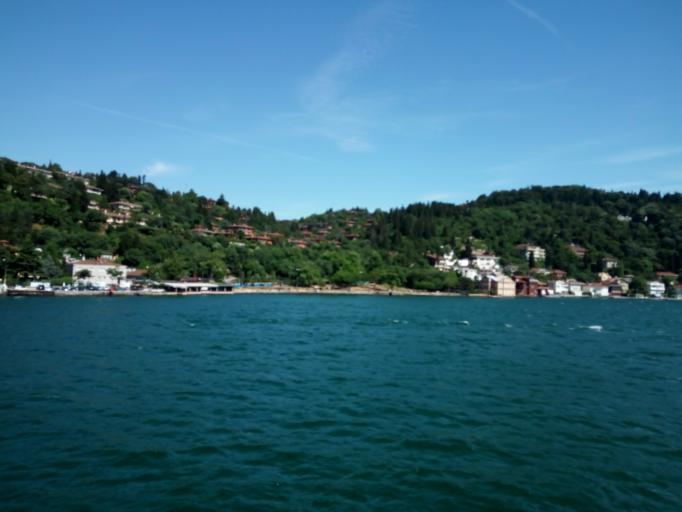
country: TR
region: Istanbul
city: UEskuedar
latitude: 41.0698
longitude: 29.0543
